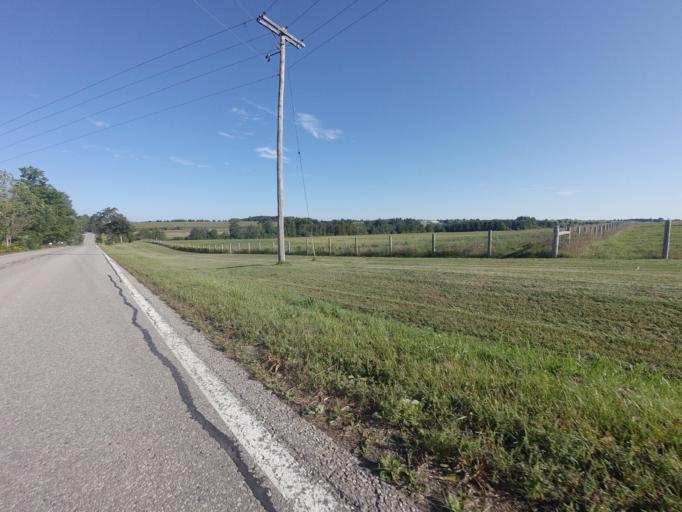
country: CA
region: Ontario
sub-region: Wellington County
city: Guelph
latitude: 43.6494
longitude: -80.4141
